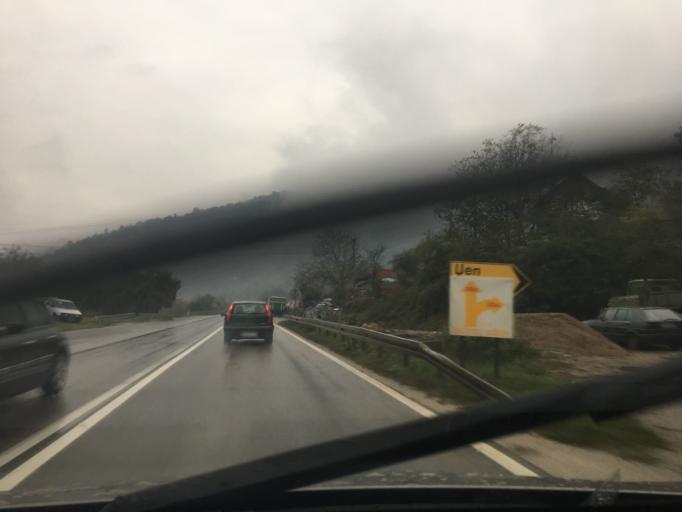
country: RS
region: Central Serbia
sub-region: Pcinjski Okrug
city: Vladicin Han
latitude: 42.7740
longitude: 22.0916
